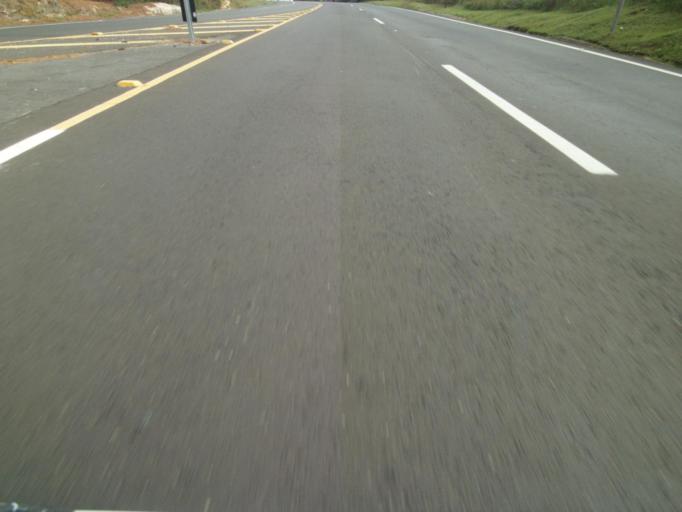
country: BR
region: Parana
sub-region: Campo Largo
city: Campo Largo
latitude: -25.4664
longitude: -49.7259
